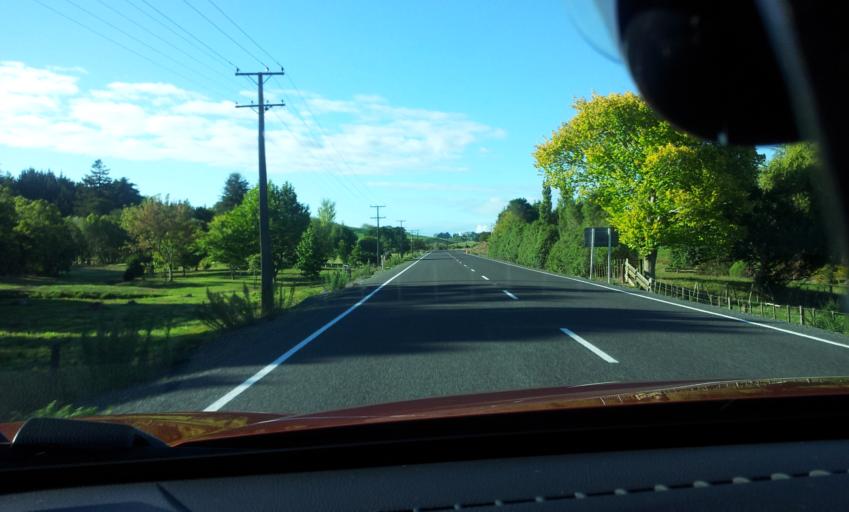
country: NZ
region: Waikato
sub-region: Hauraki District
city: Ngatea
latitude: -37.2947
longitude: 175.3738
